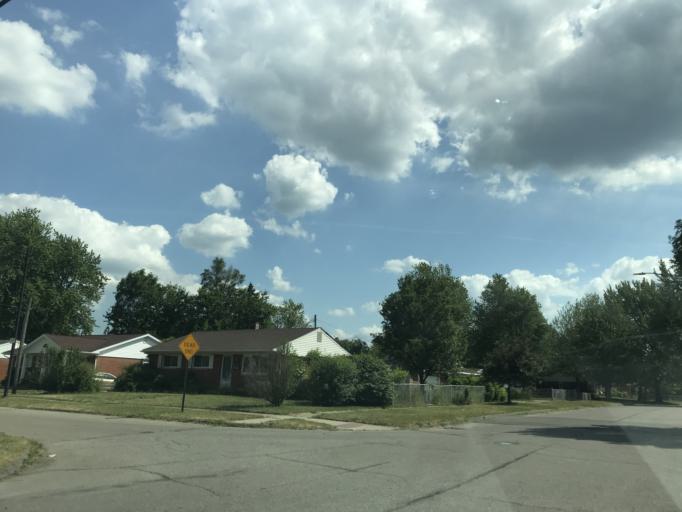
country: US
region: Michigan
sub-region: Washtenaw County
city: Ypsilanti
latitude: 42.2586
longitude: -83.5816
